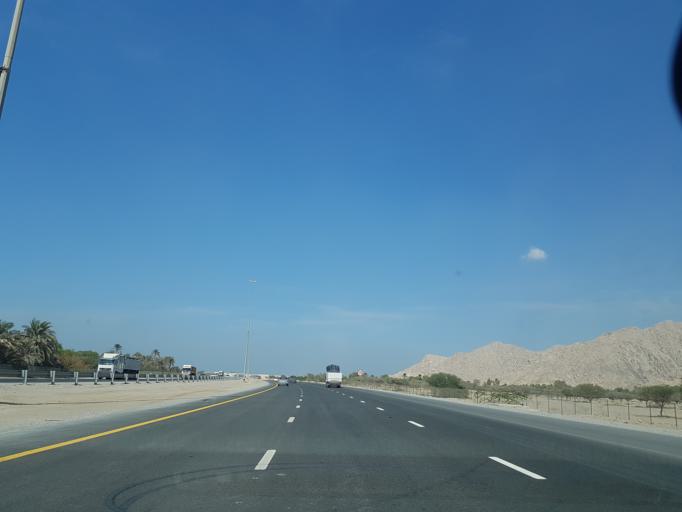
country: AE
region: Ra's al Khaymah
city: Ras al-Khaimah
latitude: 25.8091
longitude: 56.0298
